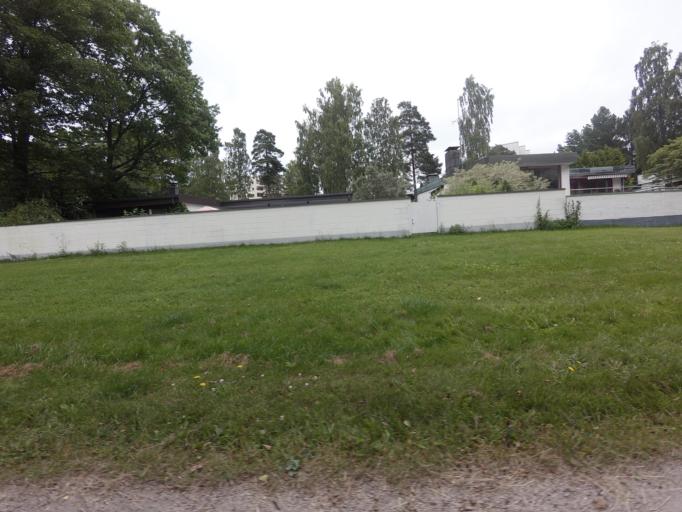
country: FI
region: Uusimaa
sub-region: Helsinki
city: Otaniemi
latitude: 60.1738
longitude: 24.8230
